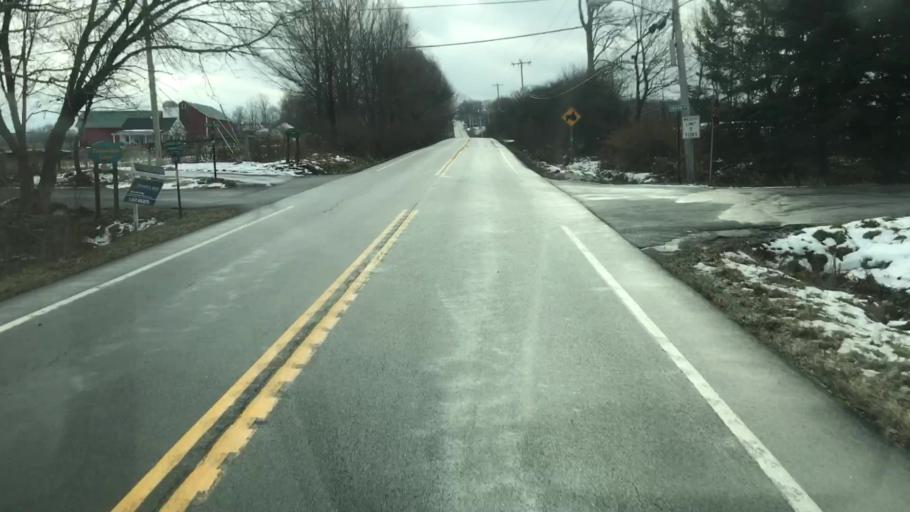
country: US
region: New York
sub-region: Onondaga County
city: Skaneateles
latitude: 42.8549
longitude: -76.3961
